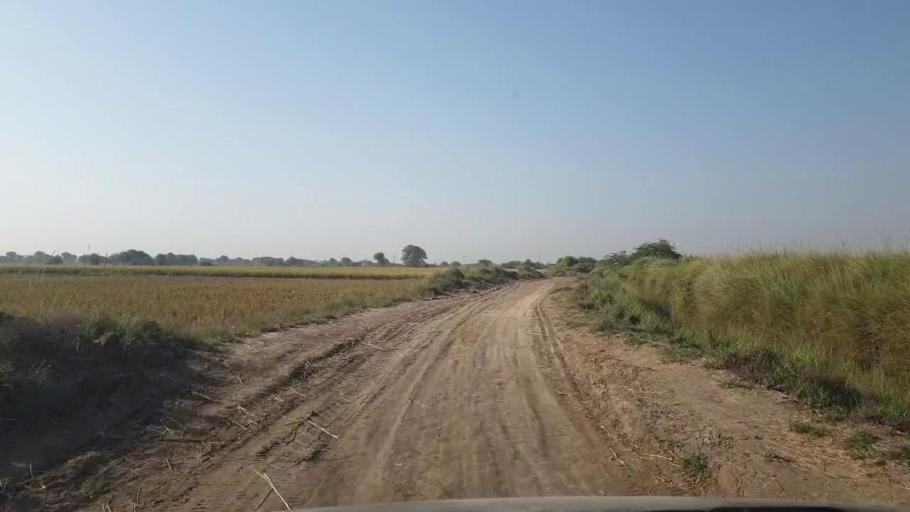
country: PK
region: Sindh
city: Badin
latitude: 24.7058
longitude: 68.7779
